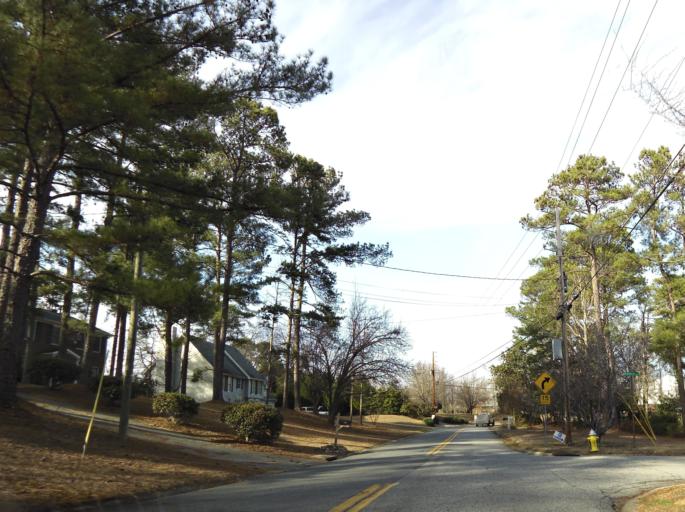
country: US
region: Georgia
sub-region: Bibb County
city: Macon
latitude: 32.8806
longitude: -83.7038
